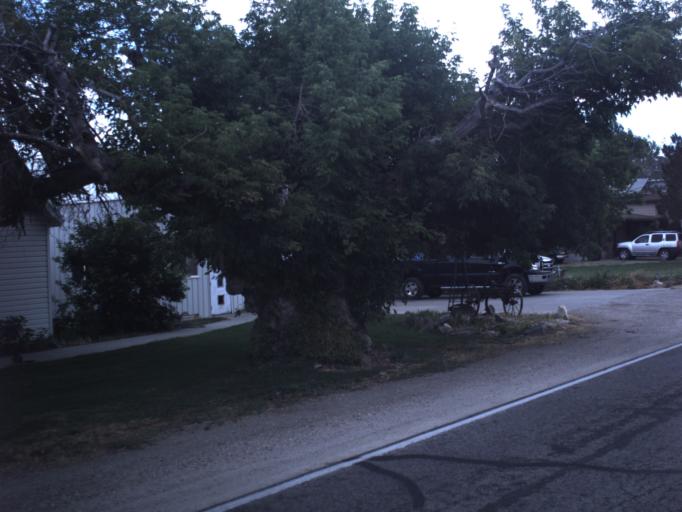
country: US
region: Utah
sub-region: Davis County
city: West Point
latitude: 41.1038
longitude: -112.1127
